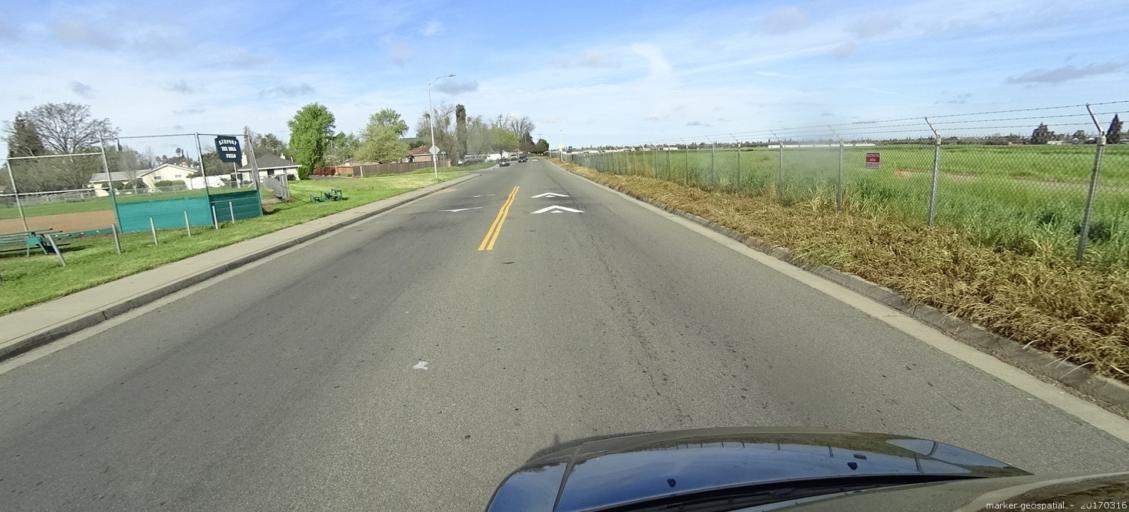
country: US
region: California
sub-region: Sacramento County
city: Parkway
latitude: 38.5094
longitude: -121.4850
